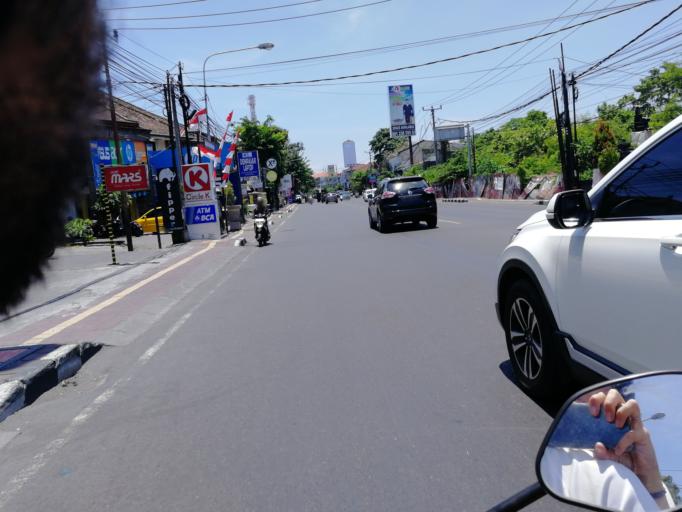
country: ID
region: Bali
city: Karyadharma
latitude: -8.6814
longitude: 115.1987
